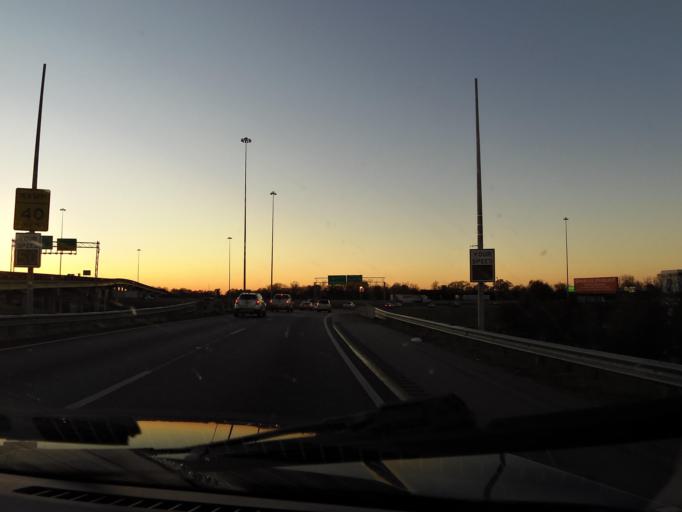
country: US
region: Alabama
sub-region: Montgomery County
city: Montgomery
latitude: 32.3677
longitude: -86.3198
